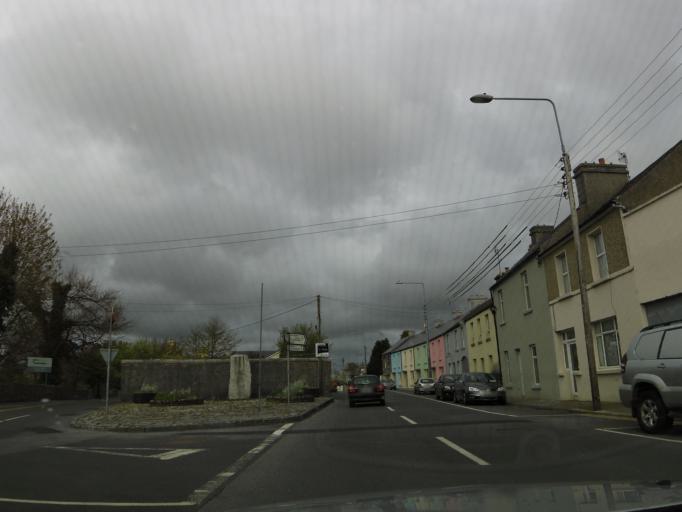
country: IE
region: Connaught
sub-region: Maigh Eo
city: Ballinrobe
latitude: 53.6250
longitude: -9.2214
